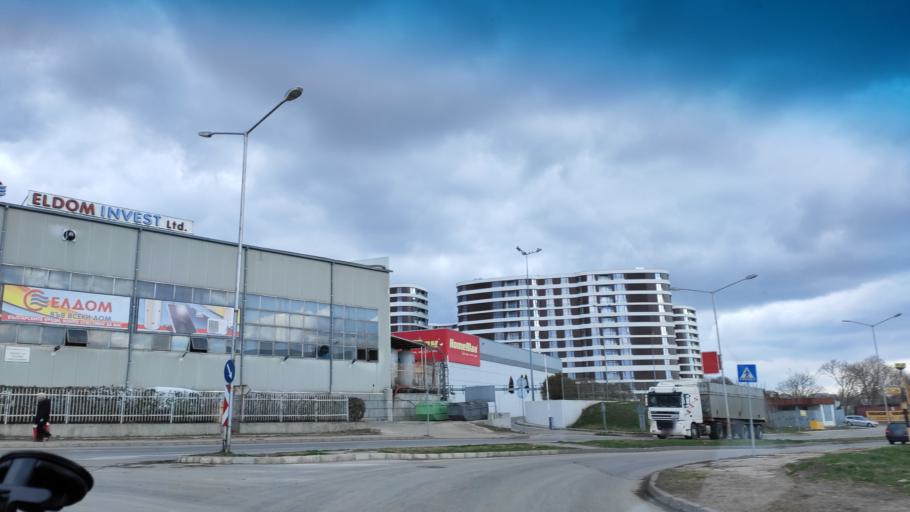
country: BG
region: Varna
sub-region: Obshtina Varna
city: Varna
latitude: 43.2194
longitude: 27.8744
